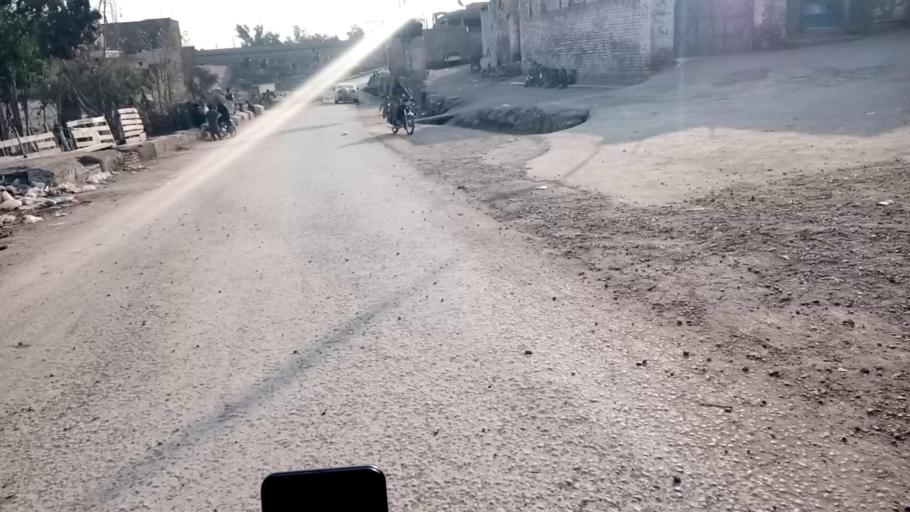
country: PK
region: Khyber Pakhtunkhwa
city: Peshawar
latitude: 34.0057
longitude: 71.4676
